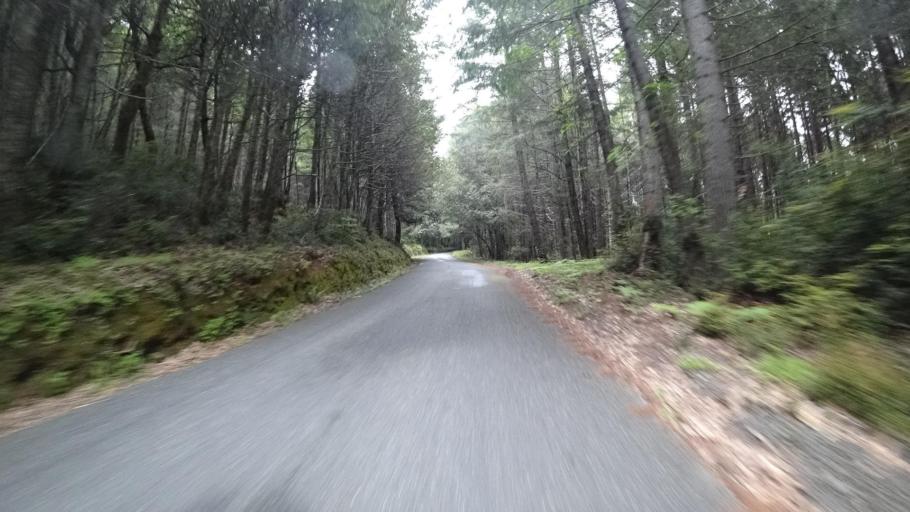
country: US
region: California
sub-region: Humboldt County
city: Willow Creek
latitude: 41.1979
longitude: -123.7589
